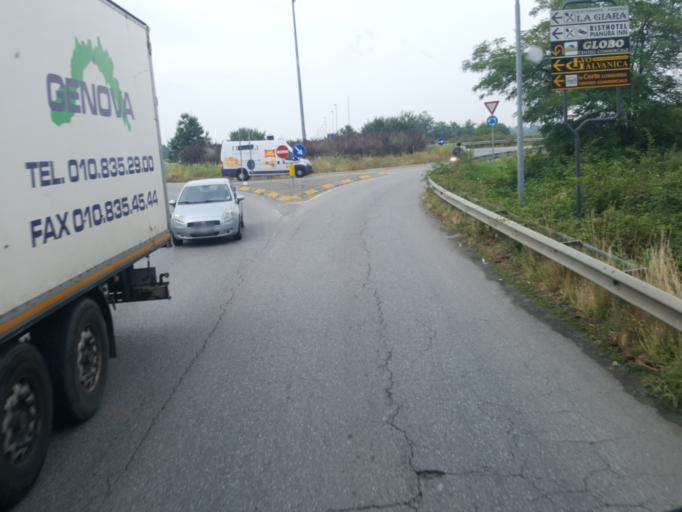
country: IT
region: Lombardy
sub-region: Provincia di Monza e Brianza
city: Cavenago di Brianza
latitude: 45.5756
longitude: 9.4134
